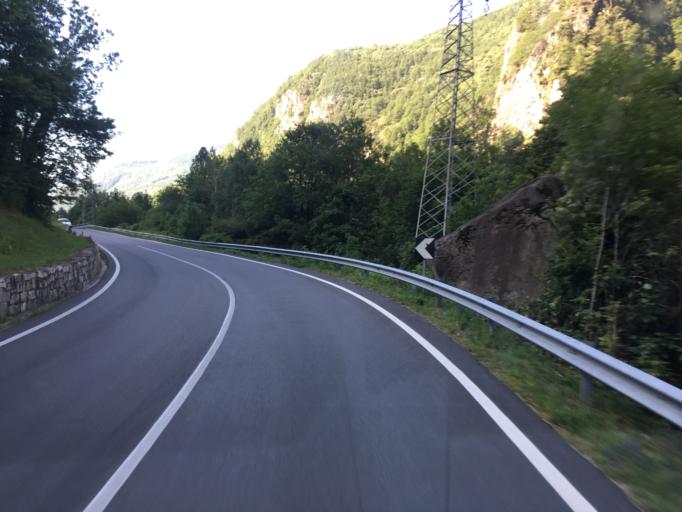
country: IT
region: Lombardy
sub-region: Provincia di Sondrio
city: San Giacomo Filippo
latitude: 46.3577
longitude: 9.3646
